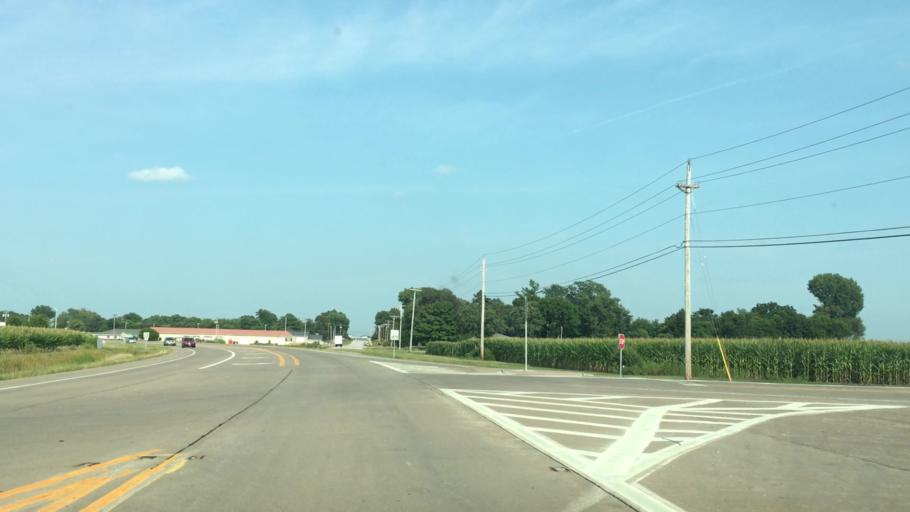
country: US
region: Illinois
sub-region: Rock Island County
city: Milan
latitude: 41.4530
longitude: -90.5307
